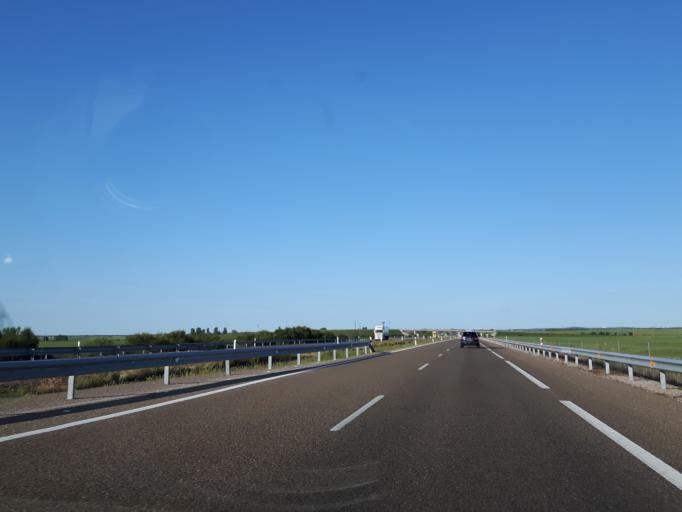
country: ES
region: Castille and Leon
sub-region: Provincia de Salamanca
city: Calzada de Don Diego
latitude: 40.8968
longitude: -5.9184
